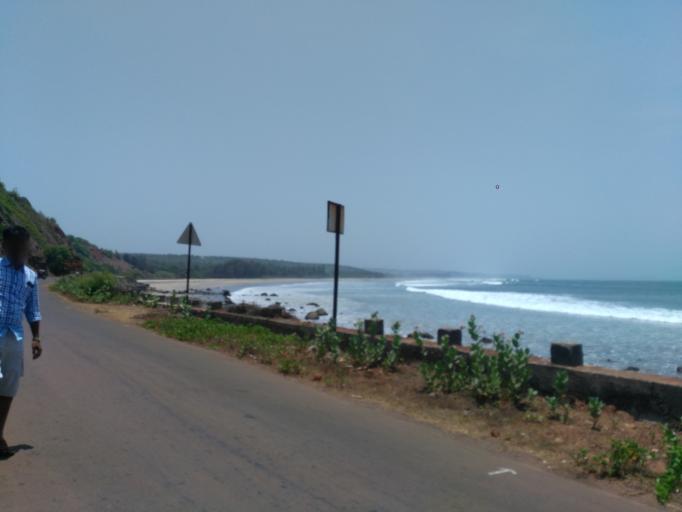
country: IN
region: Maharashtra
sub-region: Ratnagiri
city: Ratnagiri
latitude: 17.1925
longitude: 73.2490
